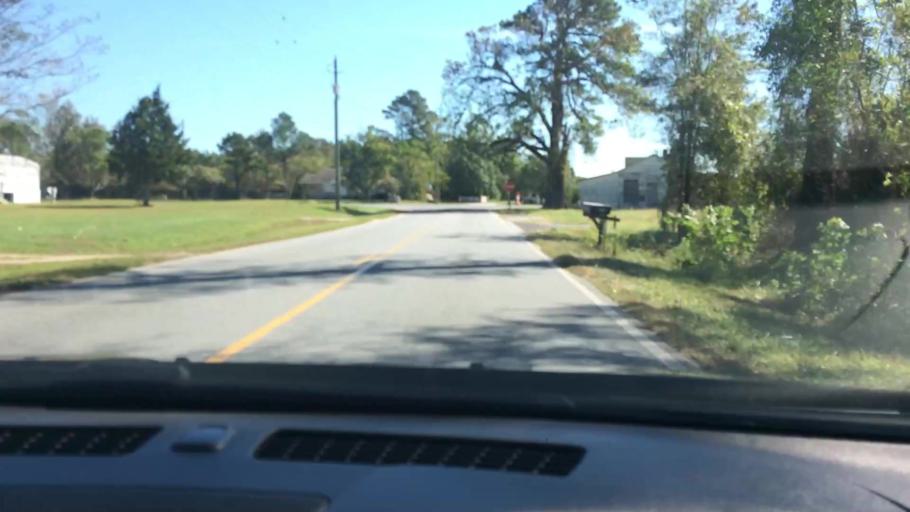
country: US
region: North Carolina
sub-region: Pitt County
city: Grifton
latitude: 35.3758
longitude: -77.3598
